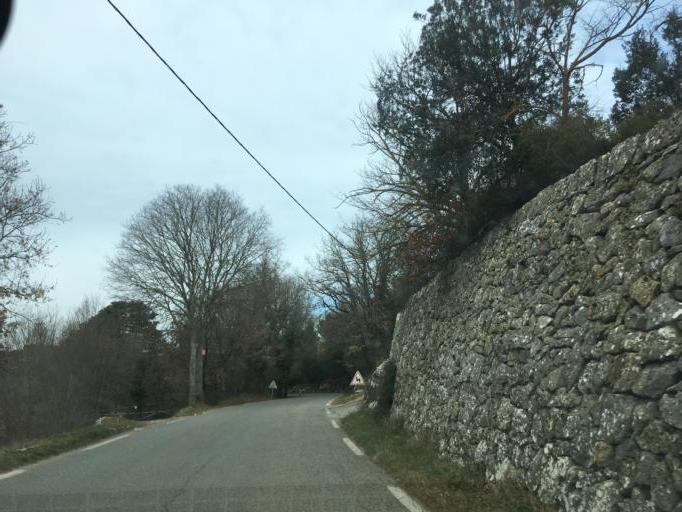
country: FR
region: Provence-Alpes-Cote d'Azur
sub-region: Departement du Var
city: Bras
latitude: 43.4670
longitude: 5.9474
